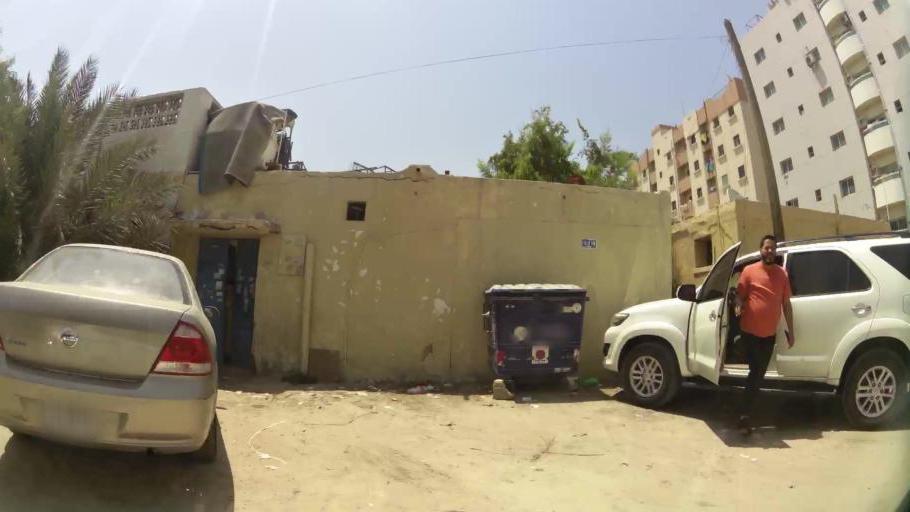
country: AE
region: Ajman
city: Ajman
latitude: 25.4032
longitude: 55.4356
